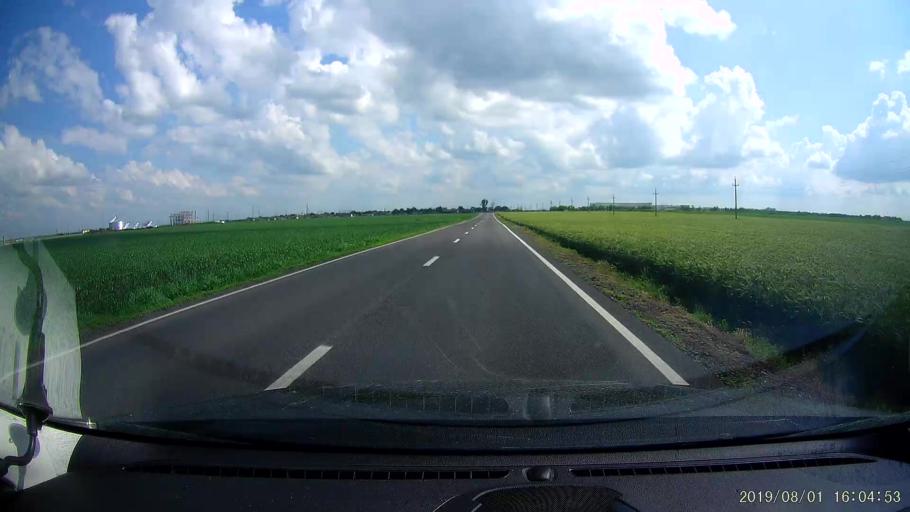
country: RO
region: Calarasi
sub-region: Comuna Dragalina
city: Drajna Noua
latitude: 44.4360
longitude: 27.3781
